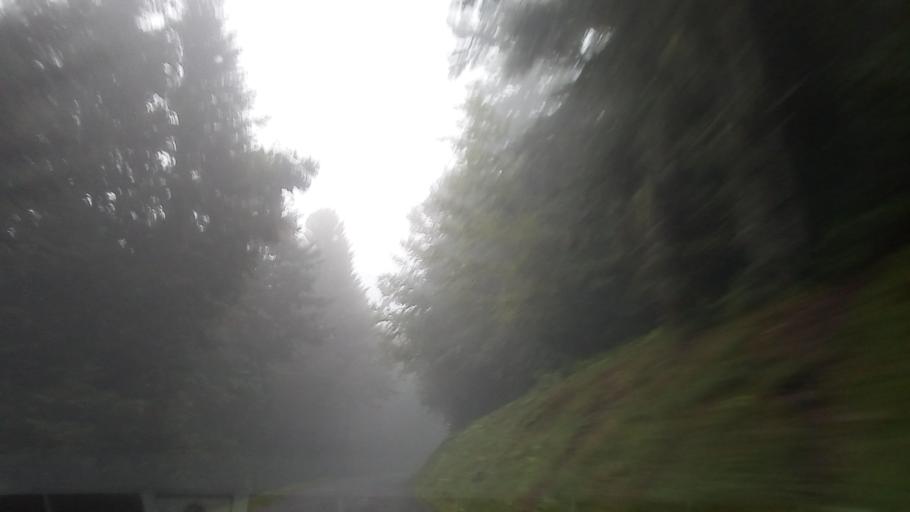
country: FR
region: Midi-Pyrenees
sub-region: Departement des Hautes-Pyrenees
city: Saint-Lary-Soulan
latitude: 42.8982
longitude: 0.3142
